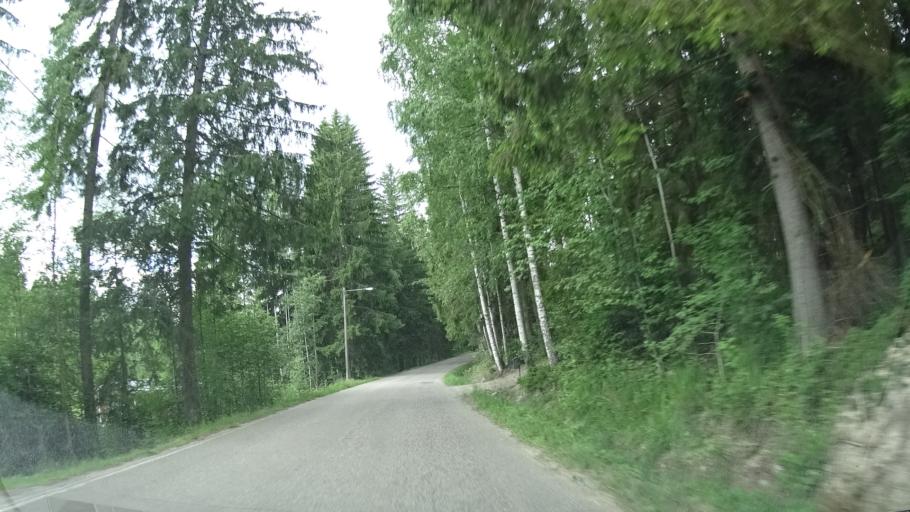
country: FI
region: Uusimaa
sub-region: Helsinki
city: Vihti
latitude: 60.4595
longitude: 24.4972
